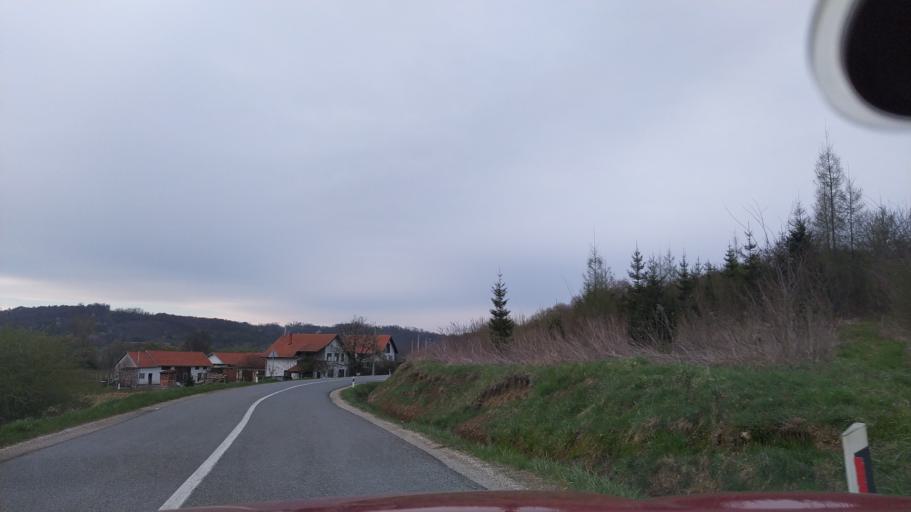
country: HR
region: Varazdinska
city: Jalzabet
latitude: 46.2133
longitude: 16.5062
